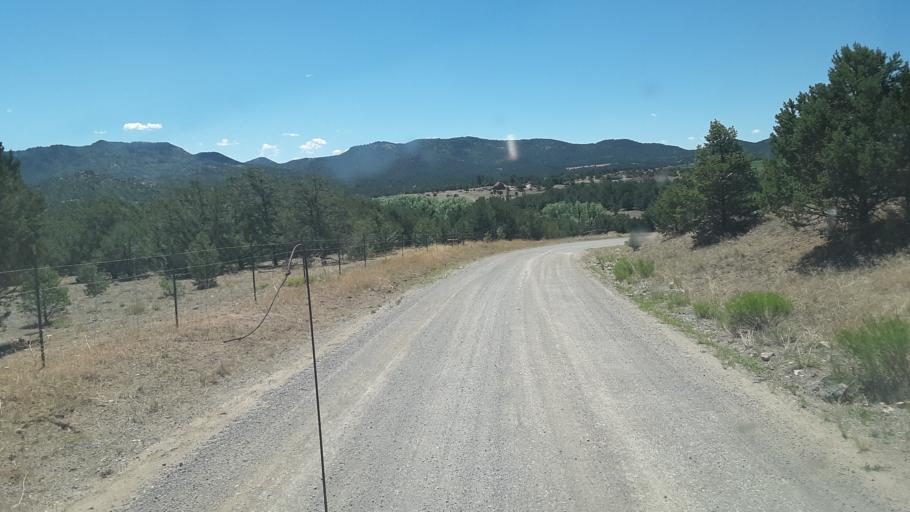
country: US
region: Colorado
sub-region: Custer County
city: Westcliffe
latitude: 38.3049
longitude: -105.6152
